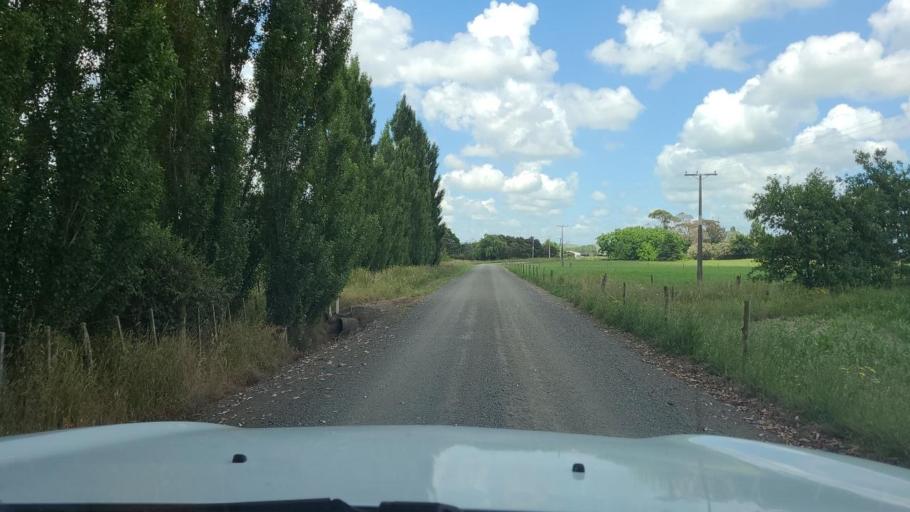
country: NZ
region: Waikato
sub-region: Hauraki District
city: Ngatea
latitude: -37.5094
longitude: 175.4409
